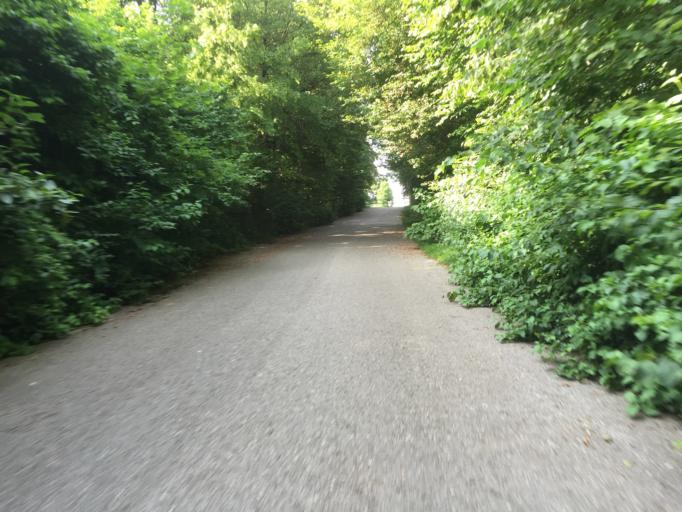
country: DE
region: Bavaria
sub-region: Upper Bavaria
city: Unterhaching
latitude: 48.1021
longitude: 11.6129
